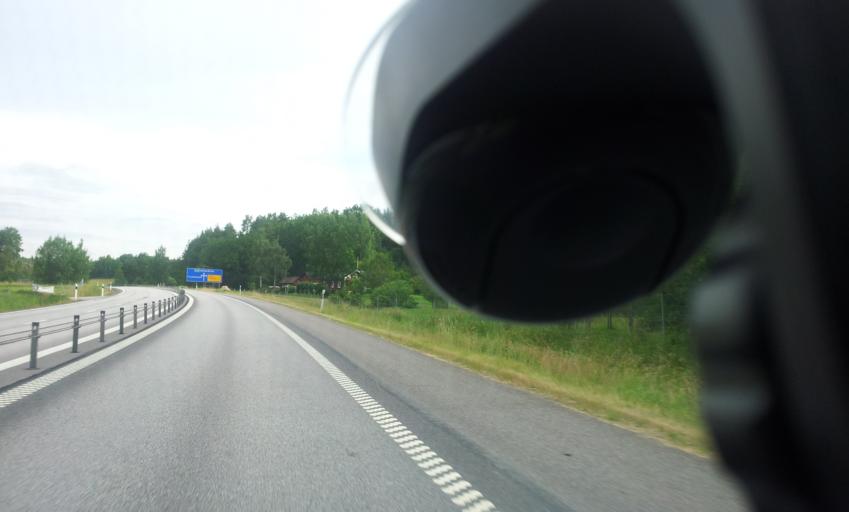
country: SE
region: OEstergoetland
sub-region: Valdemarsviks Kommun
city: Gusum
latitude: 58.3778
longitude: 16.4231
